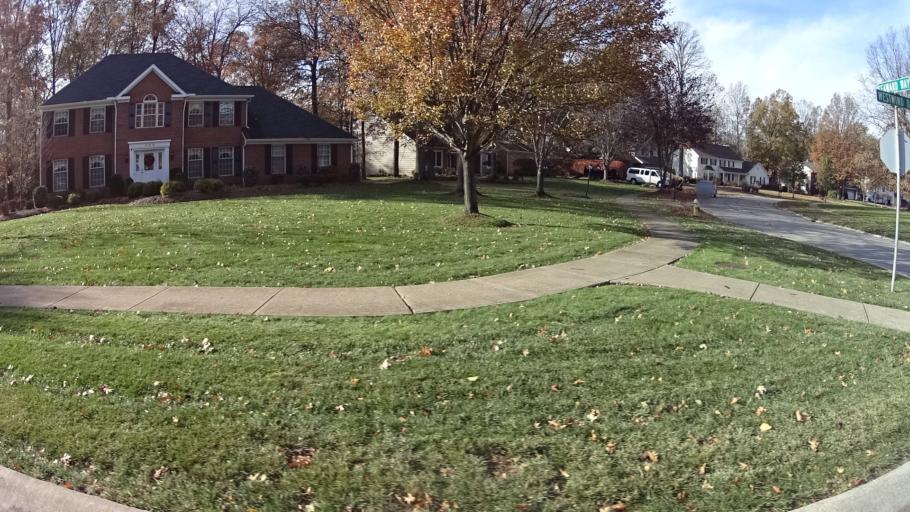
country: US
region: Ohio
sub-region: Lorain County
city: Avon Lake
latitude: 41.5023
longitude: -81.9804
